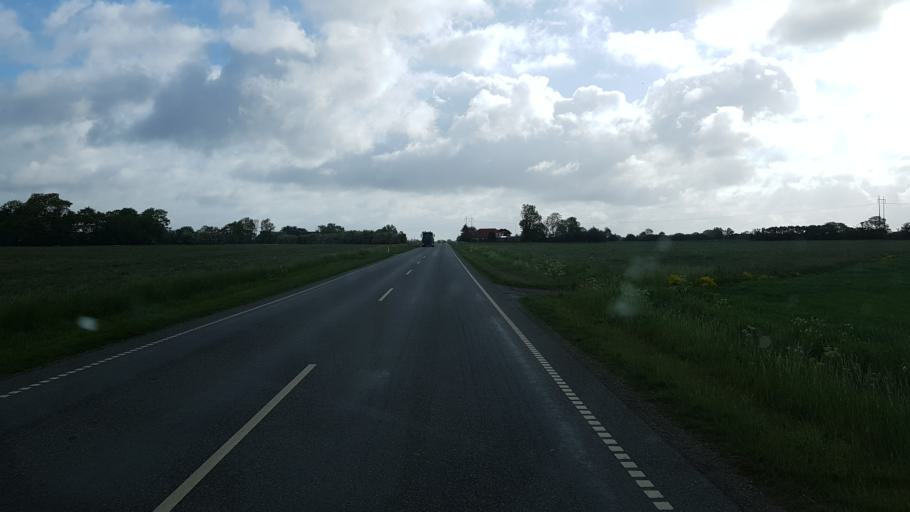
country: DK
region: South Denmark
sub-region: Vejen Kommune
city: Rodding
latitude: 55.4033
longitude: 9.1165
